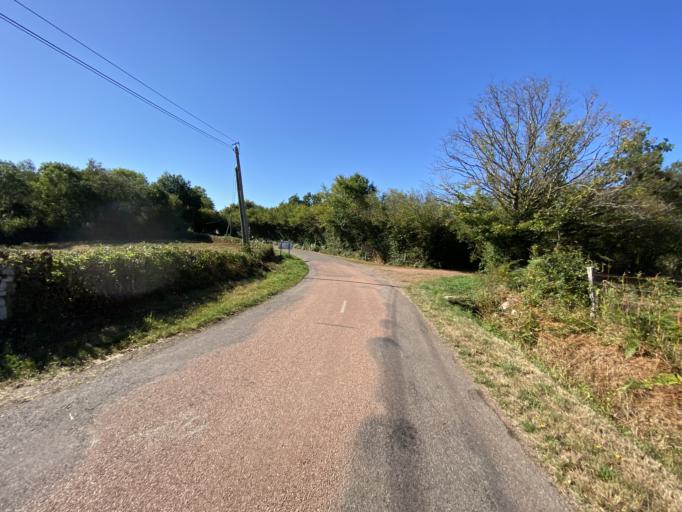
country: FR
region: Bourgogne
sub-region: Departement de la Cote-d'Or
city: Saulieu
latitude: 47.2650
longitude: 4.1749
